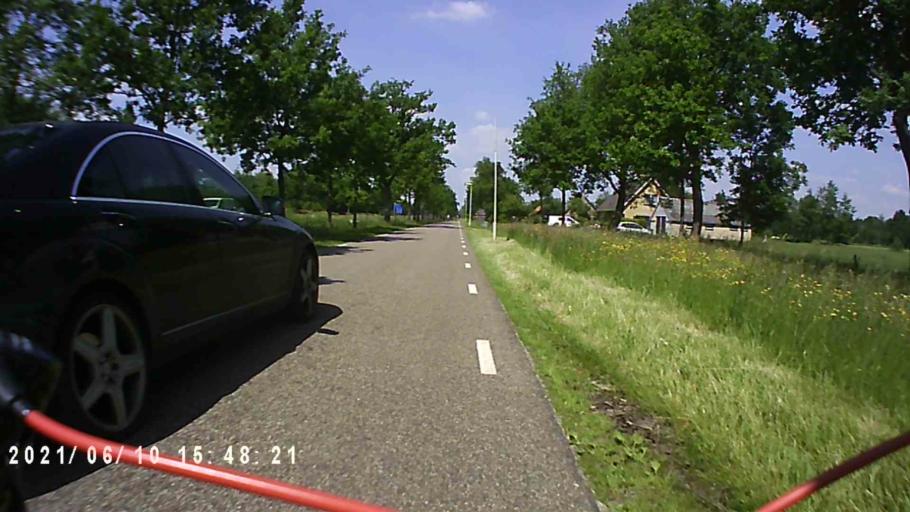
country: NL
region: Friesland
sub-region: Gemeente Smallingerland
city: Rottevalle
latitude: 53.1643
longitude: 6.1185
